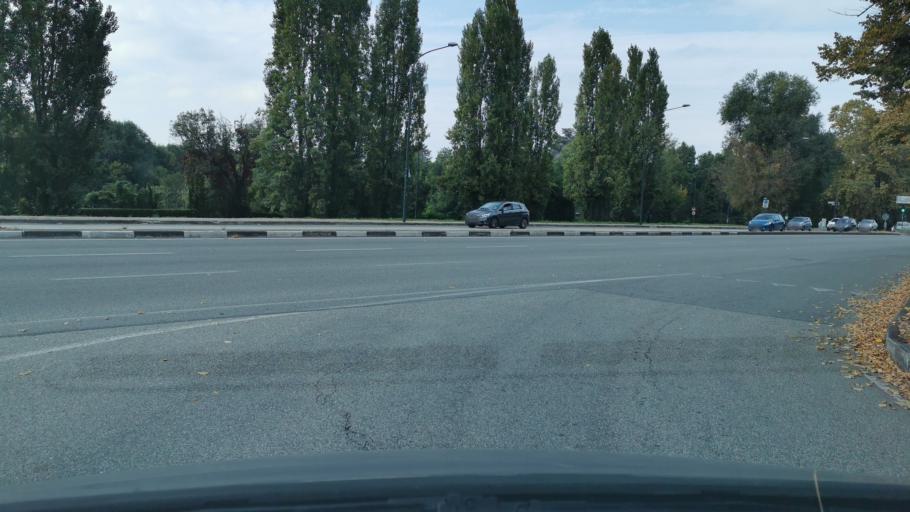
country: IT
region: Piedmont
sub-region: Provincia di Torino
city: Turin
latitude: 45.0801
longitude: 7.7296
